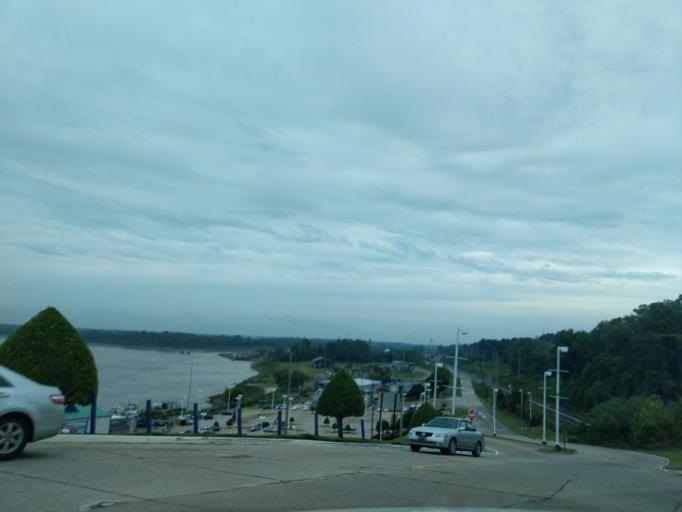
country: US
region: Mississippi
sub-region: Warren County
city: Vicksburg
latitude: 32.3230
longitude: -90.8958
